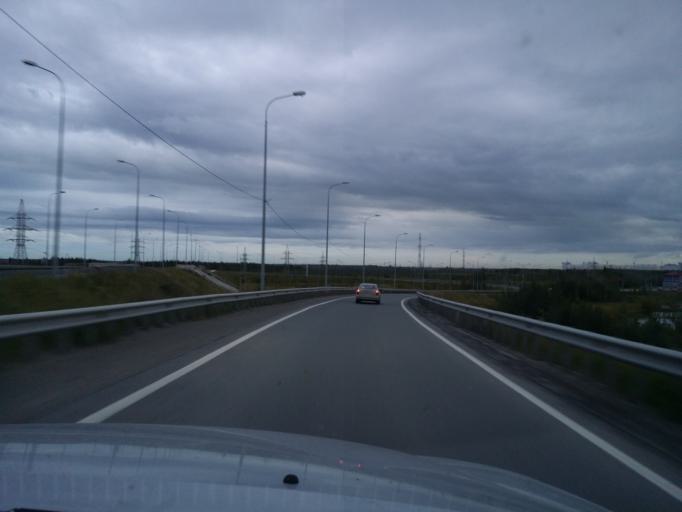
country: RU
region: Khanty-Mansiyskiy Avtonomnyy Okrug
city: Nizhnevartovsk
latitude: 60.9487
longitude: 76.6630
